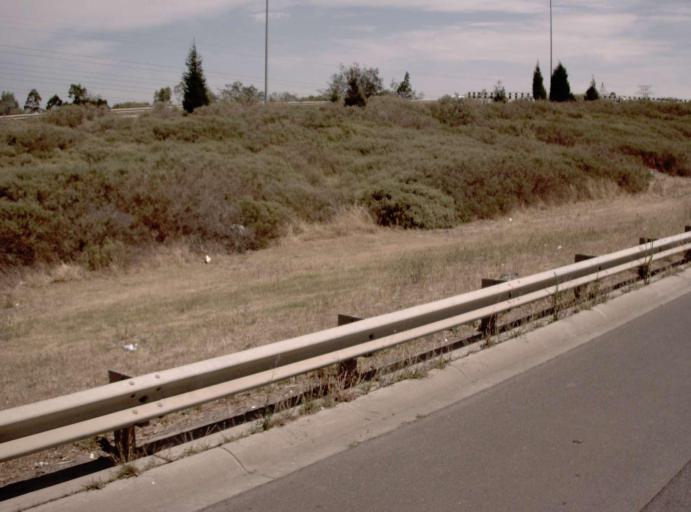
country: AU
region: Victoria
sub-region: Whittlesea
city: Thomastown
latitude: -37.6892
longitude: 144.9878
